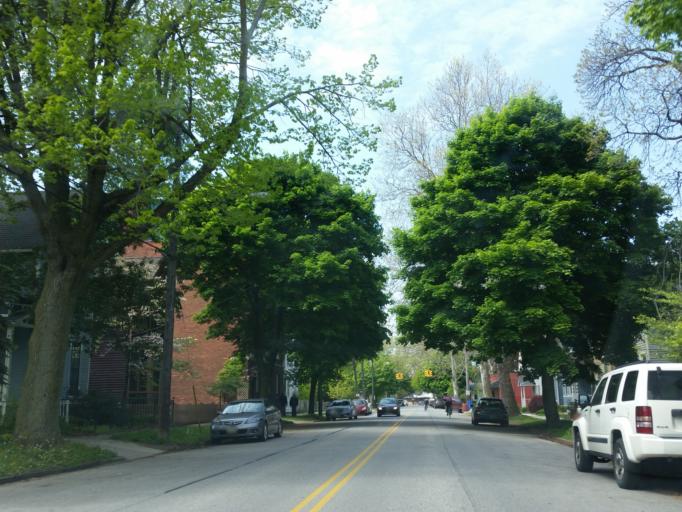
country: US
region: Ohio
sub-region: Cuyahoga County
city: Cleveland
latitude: 41.4821
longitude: -81.7133
